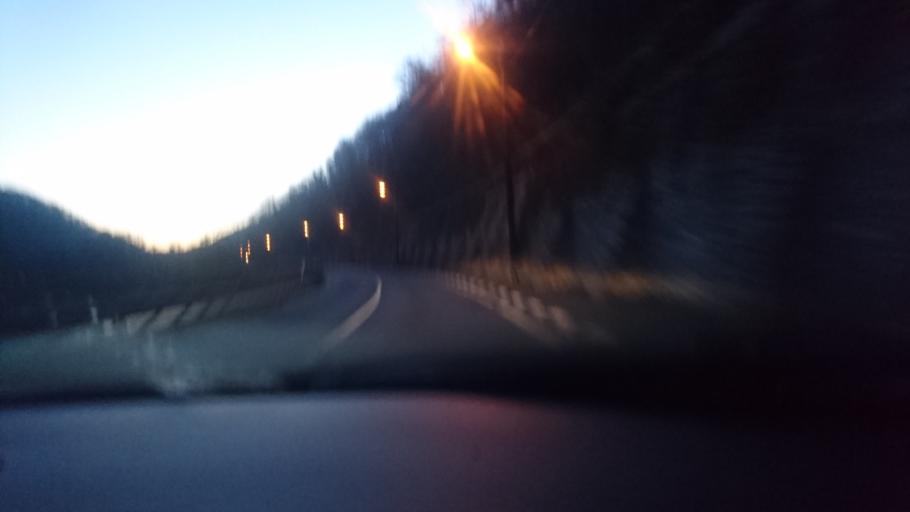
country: DE
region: Rheinland-Pfalz
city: Fachbach
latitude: 50.3395
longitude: 7.6789
